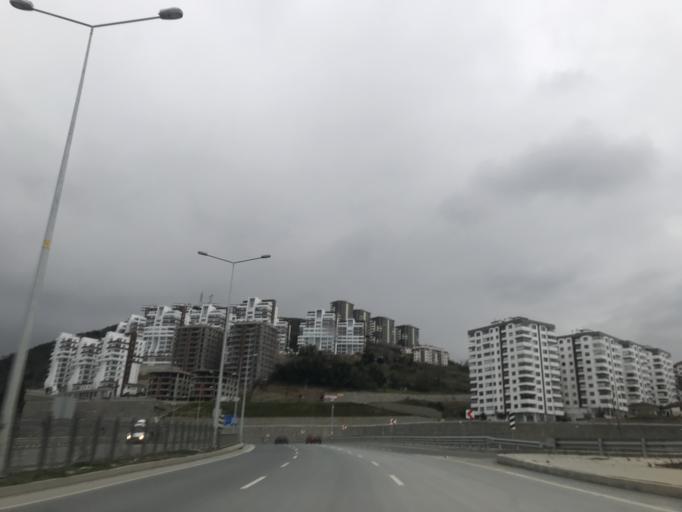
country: TR
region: Trabzon
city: Akcaabat
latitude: 41.0063
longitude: 39.6283
